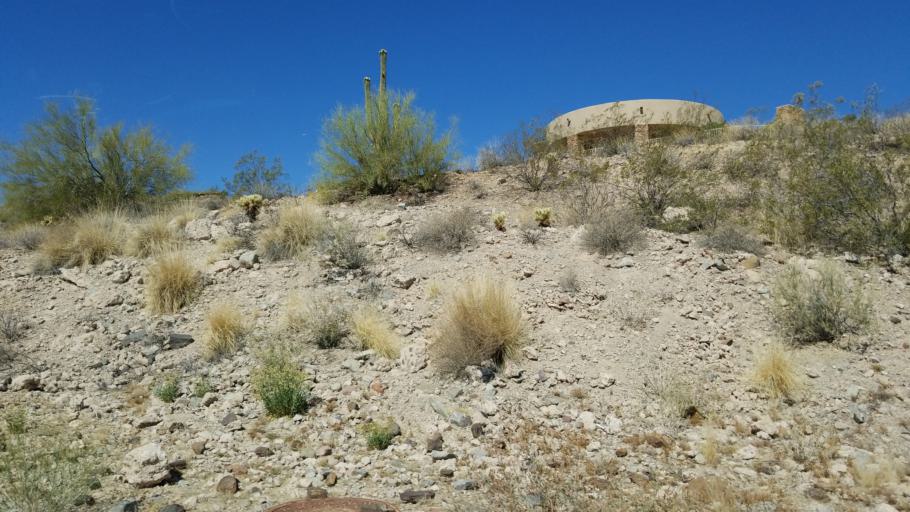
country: US
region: Arizona
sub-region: Maricopa County
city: Fountain Hills
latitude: 33.5885
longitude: -111.7558
